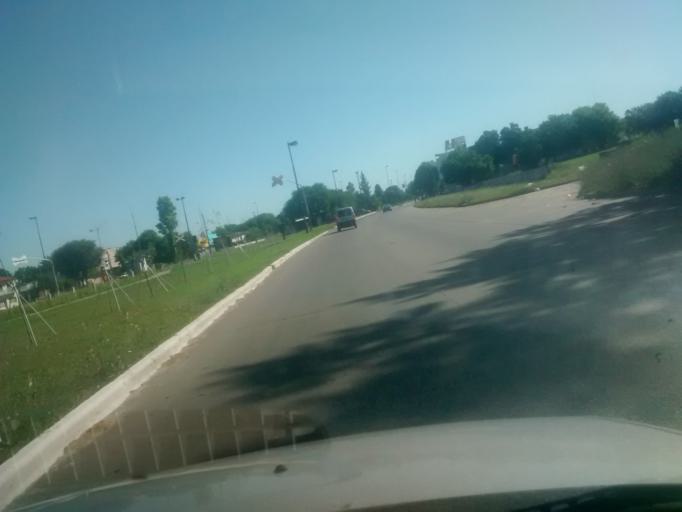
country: AR
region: Buenos Aires
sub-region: Partido de La Plata
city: La Plata
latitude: -34.9241
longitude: -57.9206
